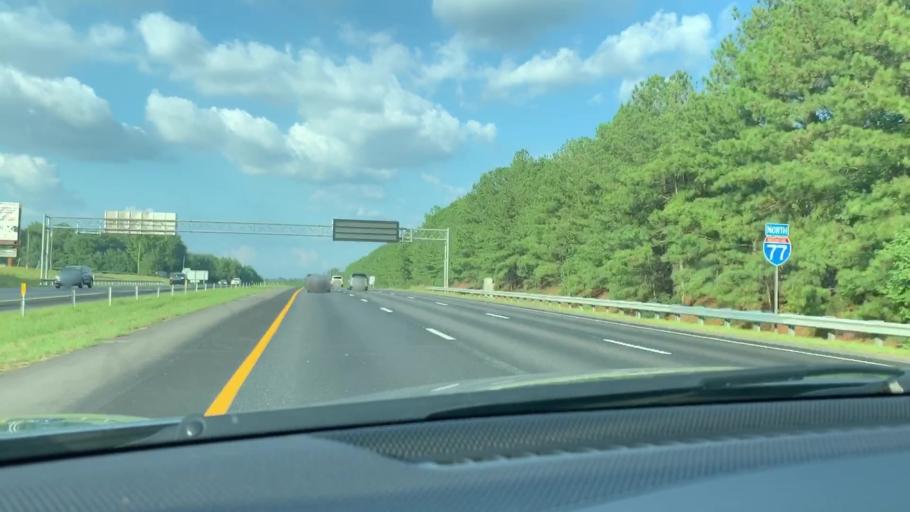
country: US
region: South Carolina
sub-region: Richland County
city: Woodfield
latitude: 34.0287
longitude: -80.9418
